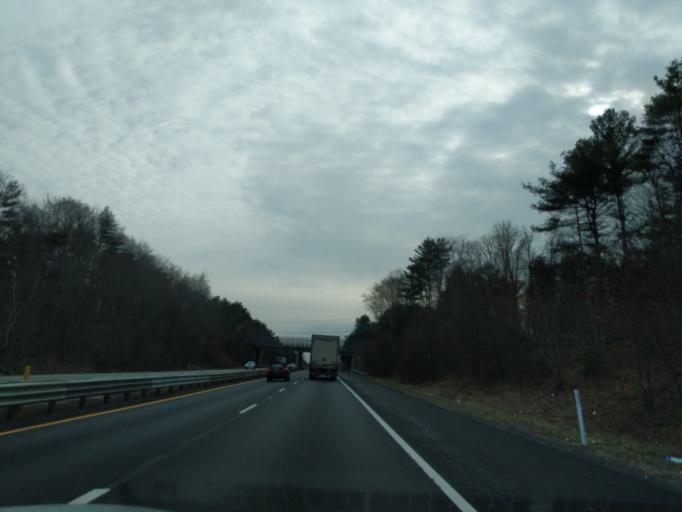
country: US
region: Massachusetts
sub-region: Bristol County
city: Raynham Center
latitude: 41.9115
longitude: -71.0393
